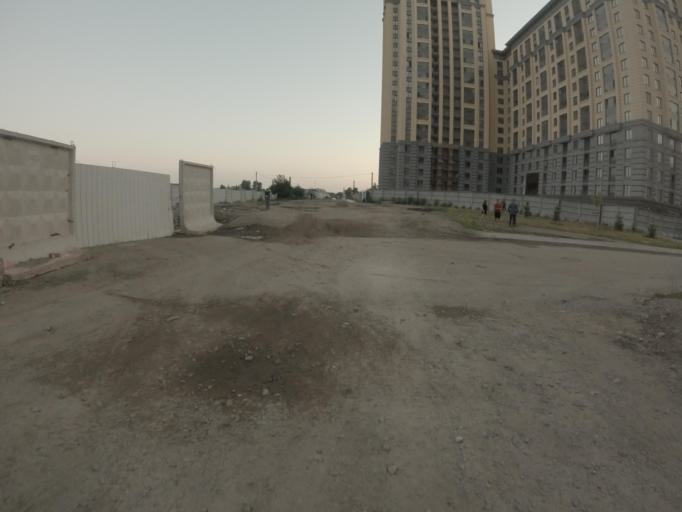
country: RU
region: St.-Petersburg
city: Obukhovo
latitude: 59.8990
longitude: 30.4488
